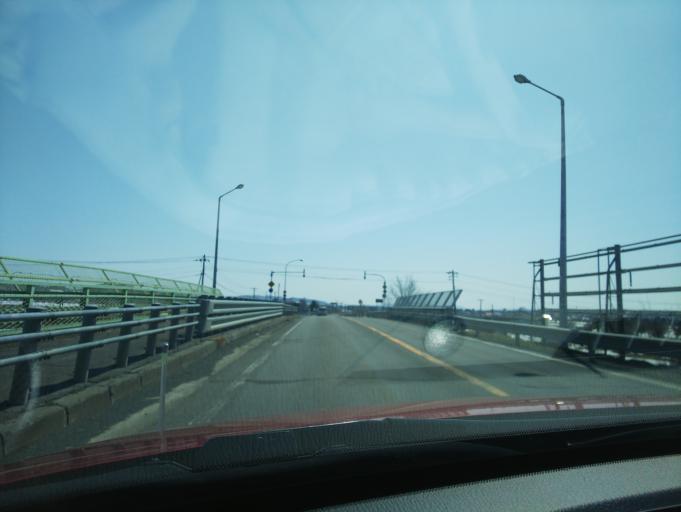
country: JP
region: Hokkaido
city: Nayoro
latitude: 44.1965
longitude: 142.3950
